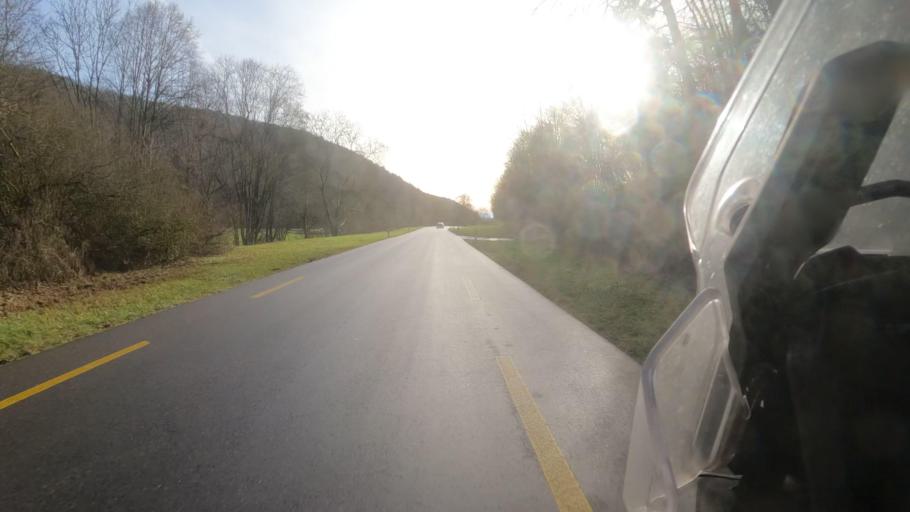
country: CH
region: Schaffhausen
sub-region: Bezirk Reiat
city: Stetten
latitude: 47.7473
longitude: 8.6171
